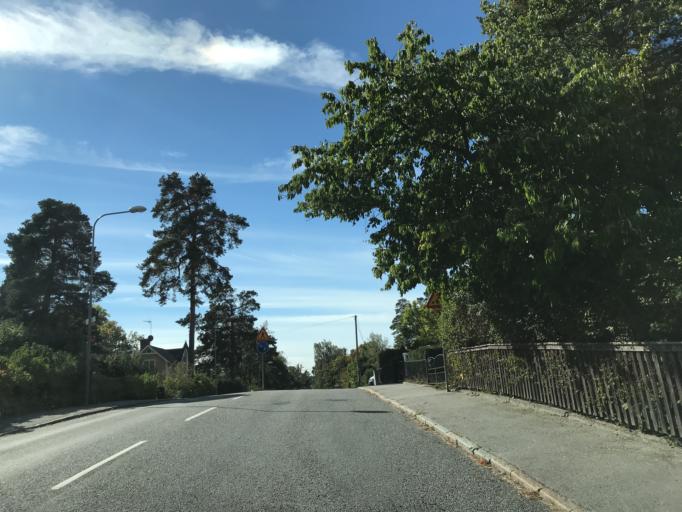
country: SE
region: Stockholm
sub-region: Huddinge Kommun
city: Huddinge
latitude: 59.2758
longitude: 17.9929
